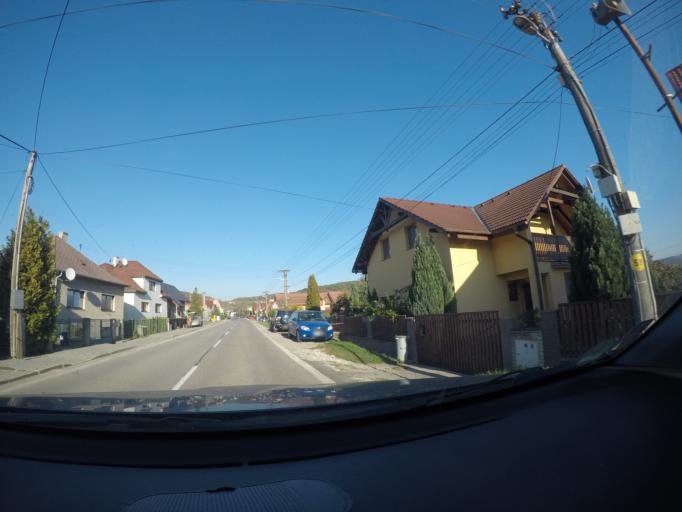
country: SK
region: Trenciansky
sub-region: Okres Trencin
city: Trencin
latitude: 48.9066
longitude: 18.0458
